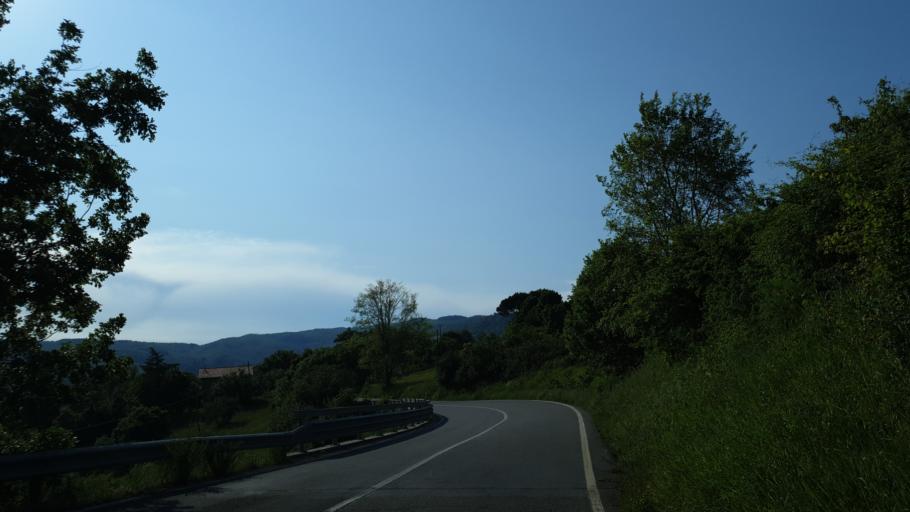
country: IT
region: Tuscany
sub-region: Province of Arezzo
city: Strada
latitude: 43.7588
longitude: 11.7135
